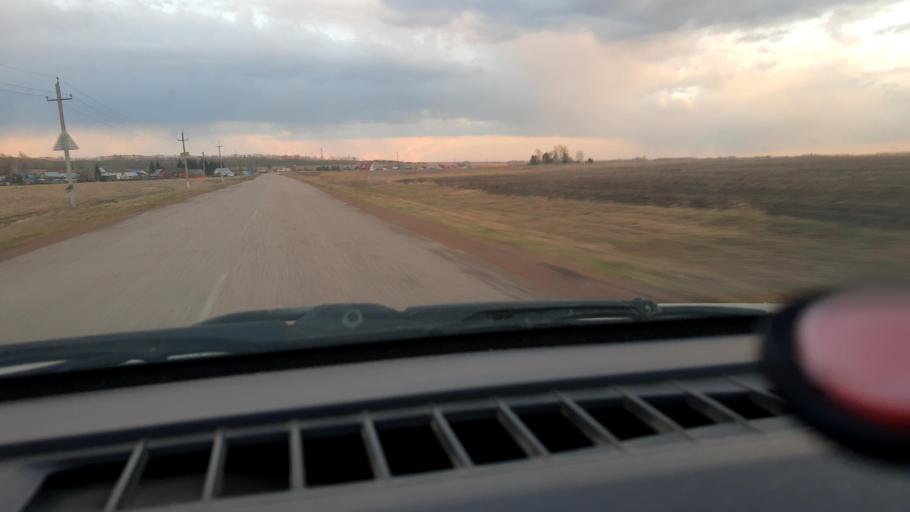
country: RU
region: Bashkortostan
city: Asanovo
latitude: 54.9321
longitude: 55.5176
